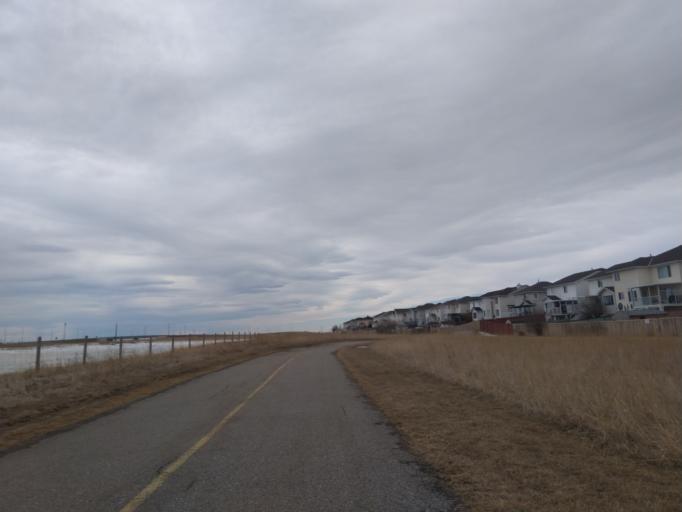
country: CA
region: Alberta
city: Chestermere
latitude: 51.1056
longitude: -113.9224
